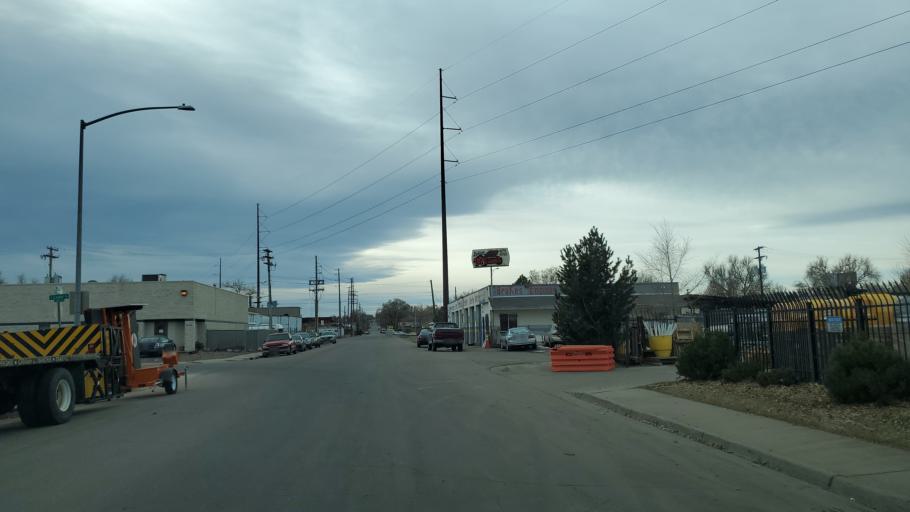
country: US
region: Colorado
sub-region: Denver County
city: Denver
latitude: 39.7134
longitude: -105.0040
